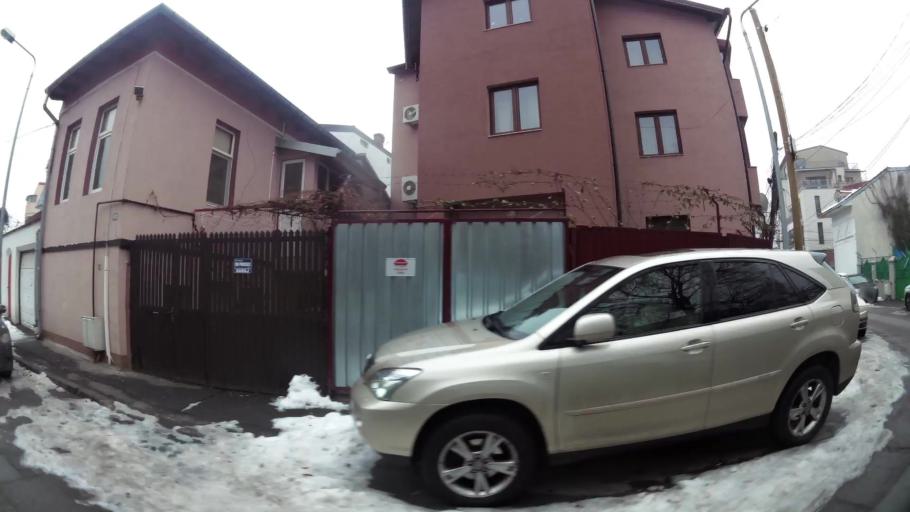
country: RO
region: Bucuresti
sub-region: Municipiul Bucuresti
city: Bucharest
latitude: 44.4510
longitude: 26.1101
